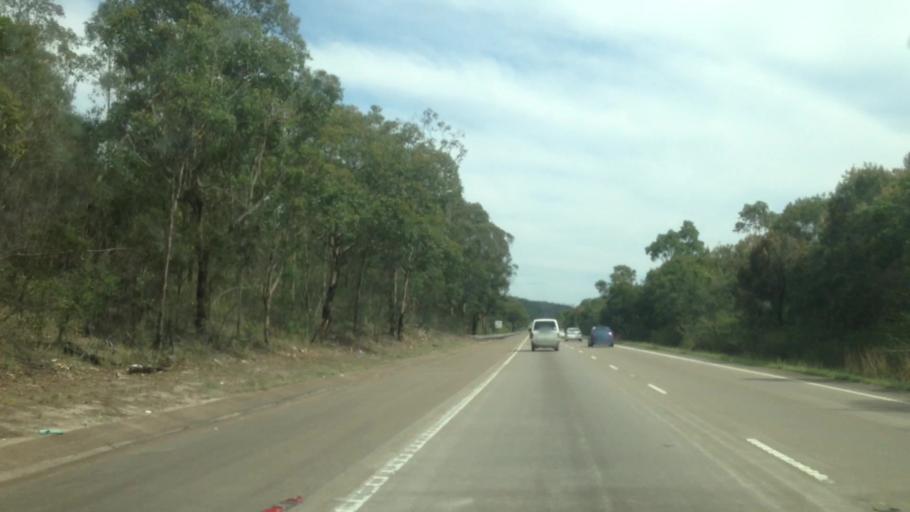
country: AU
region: New South Wales
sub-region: Lake Macquarie Shire
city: Fennell Bay
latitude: -32.9626
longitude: 151.5393
